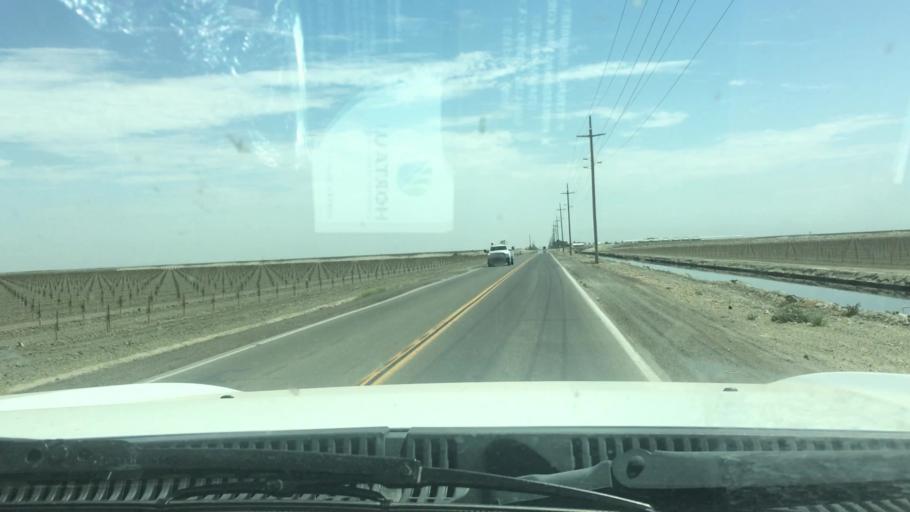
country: US
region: California
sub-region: Kings County
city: Corcoran
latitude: 36.0495
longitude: -119.5721
